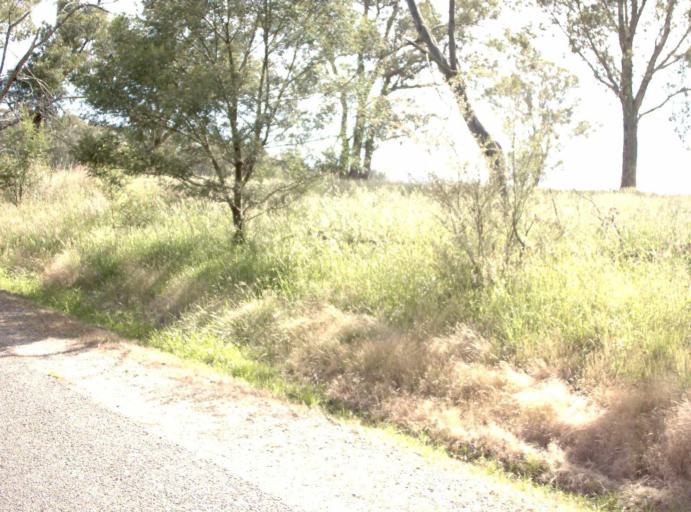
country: AU
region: Victoria
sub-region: East Gippsland
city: Lakes Entrance
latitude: -37.4850
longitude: 148.1280
